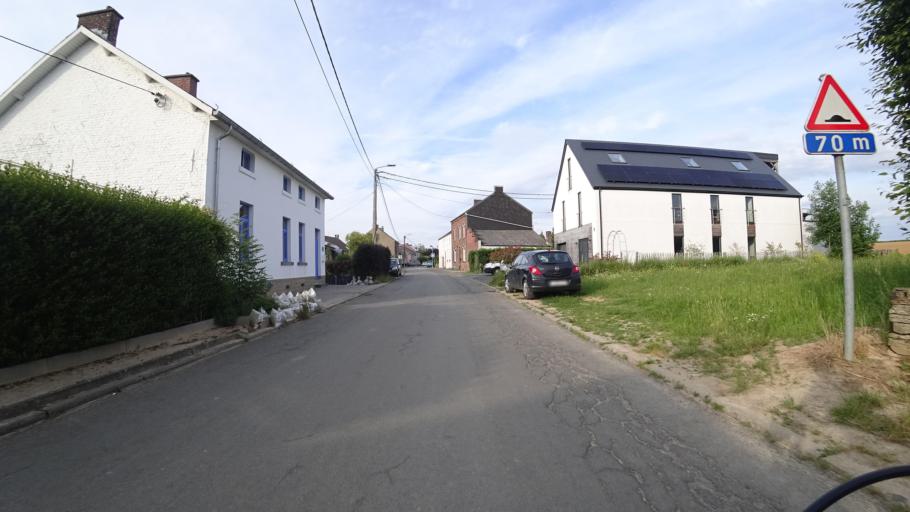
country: BE
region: Wallonia
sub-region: Province de Namur
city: Gembloux
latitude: 50.5753
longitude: 4.7168
